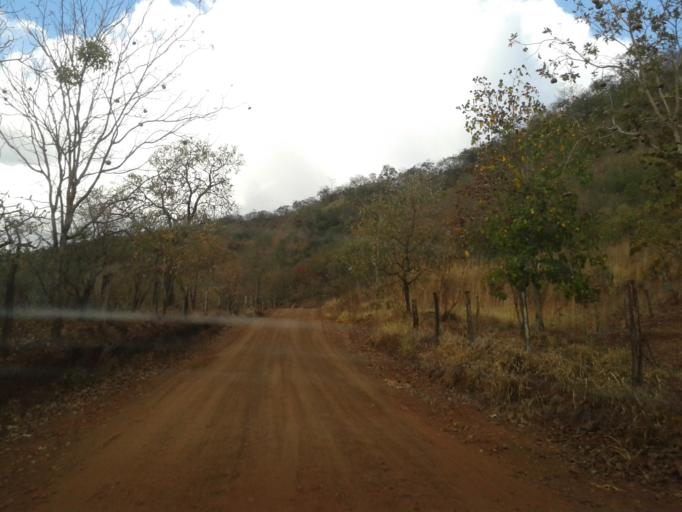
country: BR
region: Minas Gerais
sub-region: Santa Vitoria
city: Santa Vitoria
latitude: -19.2027
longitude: -49.8843
